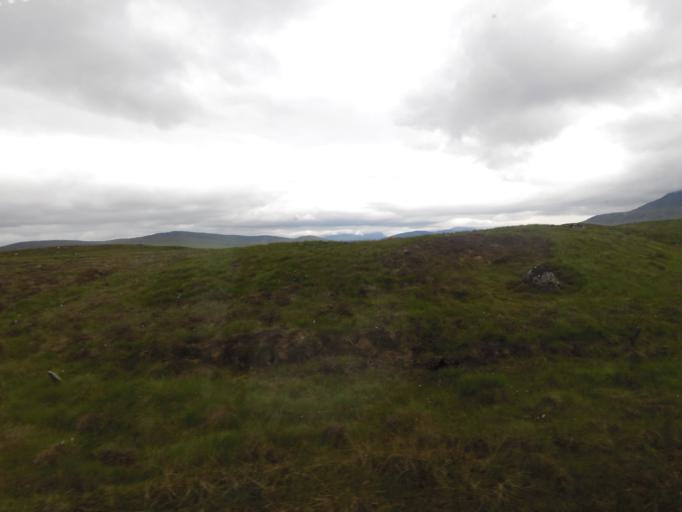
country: GB
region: Scotland
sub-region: Highland
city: Spean Bridge
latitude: 56.7277
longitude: -4.6414
